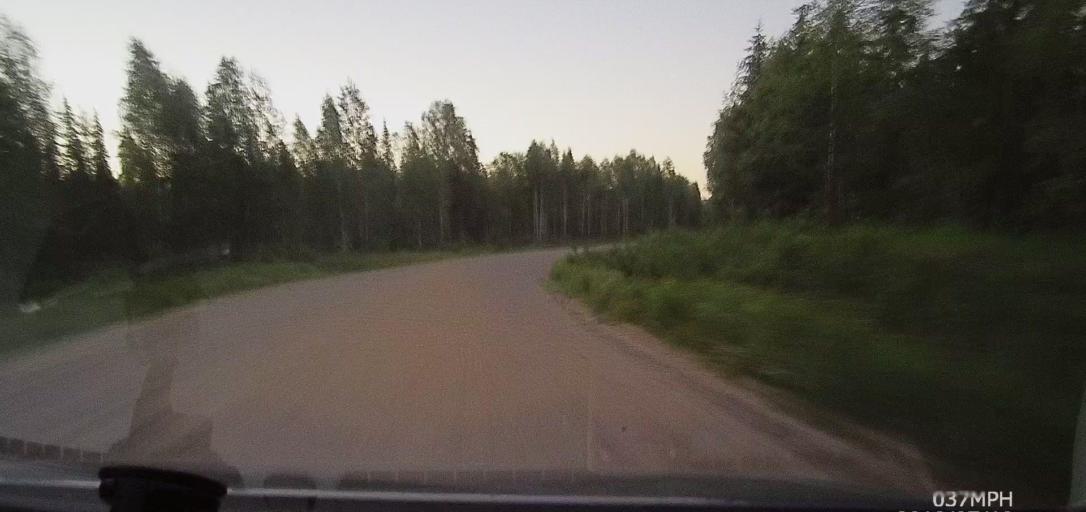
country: RU
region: Arkhangelskaya
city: Pinega
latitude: 64.4336
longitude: 43.1359
